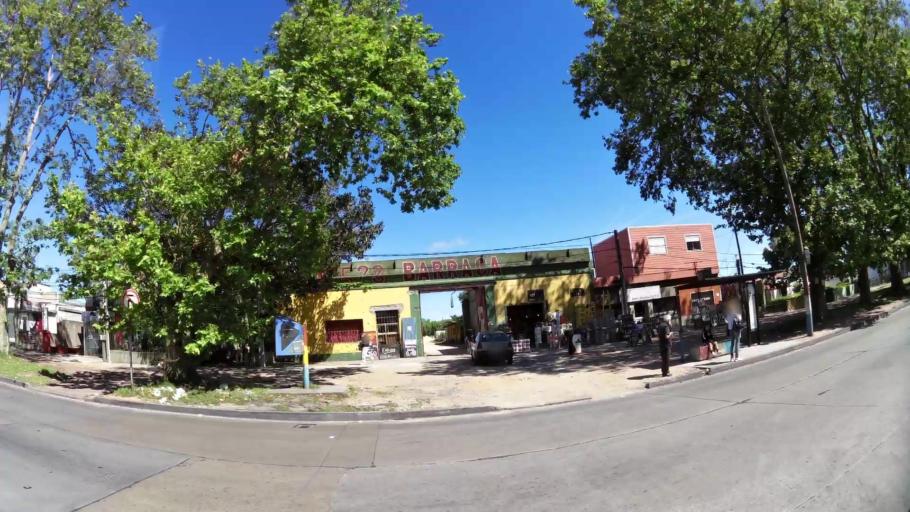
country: UY
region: Canelones
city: Paso de Carrasco
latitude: -34.8513
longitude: -56.1285
